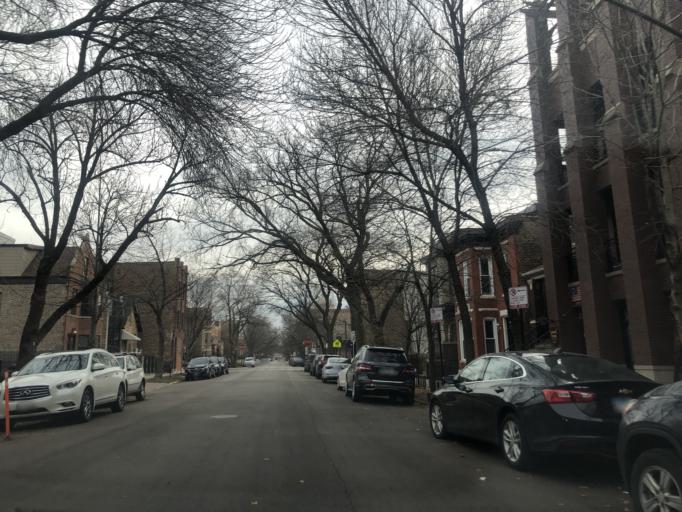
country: US
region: Illinois
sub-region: Cook County
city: Chicago
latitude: 41.9159
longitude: -87.6774
